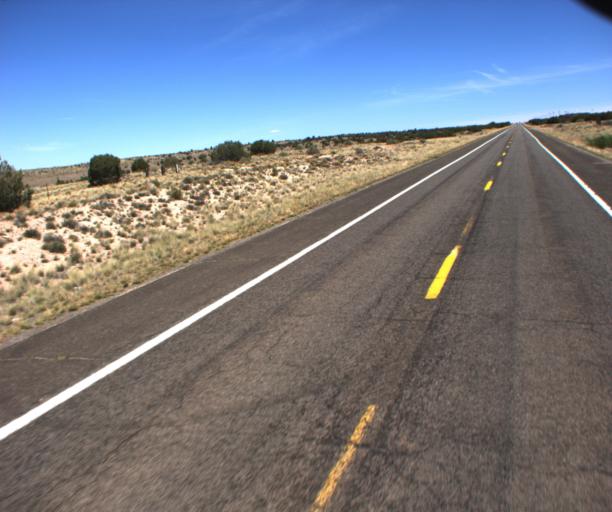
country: US
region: Arizona
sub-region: Mohave County
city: Peach Springs
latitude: 35.4954
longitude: -113.5416
